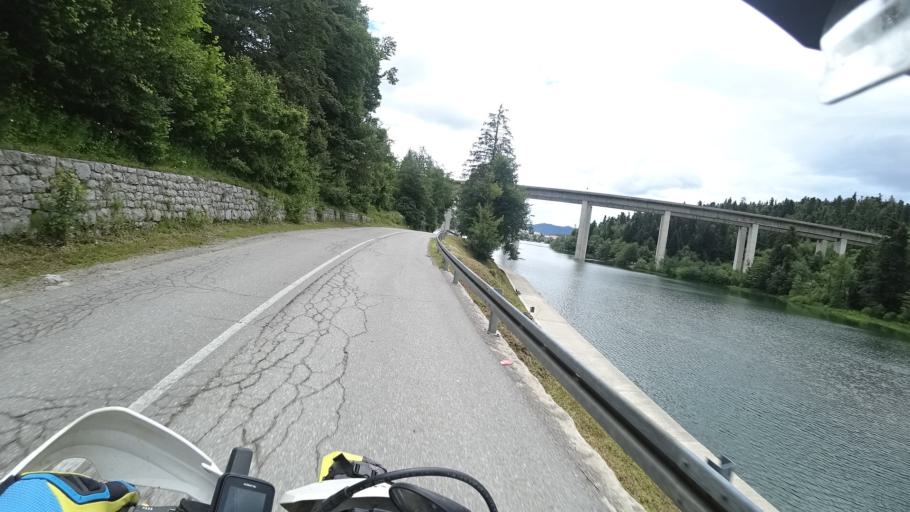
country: HR
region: Primorsko-Goranska
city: Hreljin
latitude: 45.3190
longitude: 14.7094
